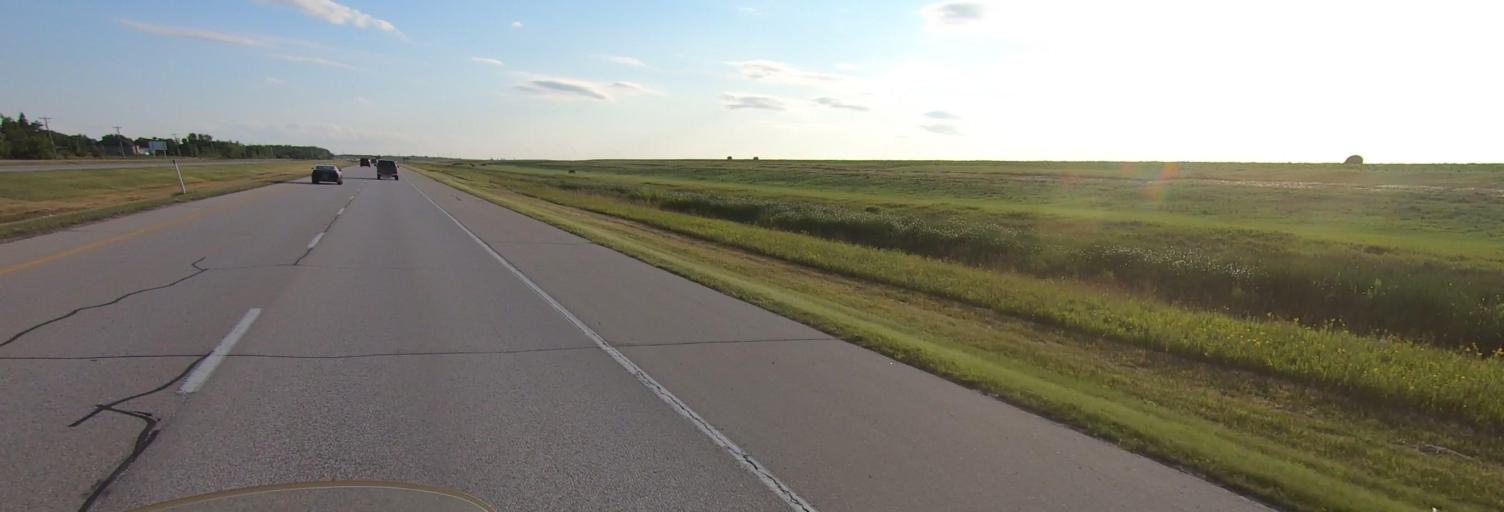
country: CA
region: Manitoba
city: Selkirk
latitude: 50.0039
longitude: -96.9623
